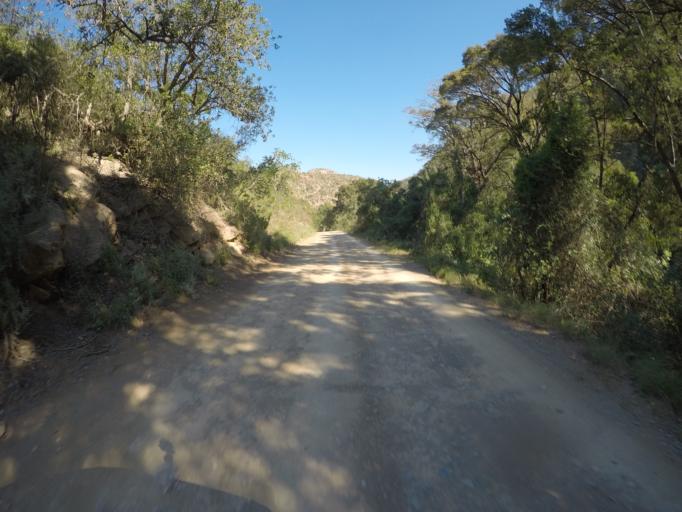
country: ZA
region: Eastern Cape
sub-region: Cacadu District Municipality
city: Kareedouw
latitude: -33.6604
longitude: 24.5381
